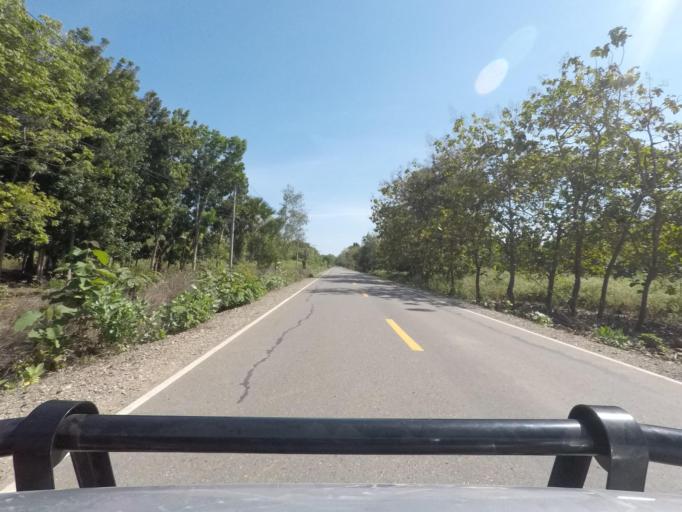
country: TL
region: Bobonaro
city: Maliana
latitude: -8.8936
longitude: 125.0105
